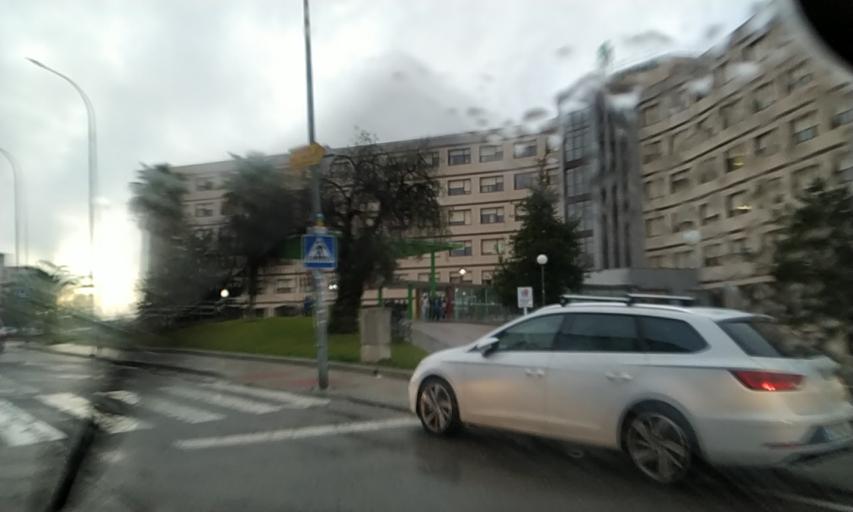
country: ES
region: Extremadura
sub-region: Provincia de Badajoz
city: Merida
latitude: 38.9120
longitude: -6.3631
